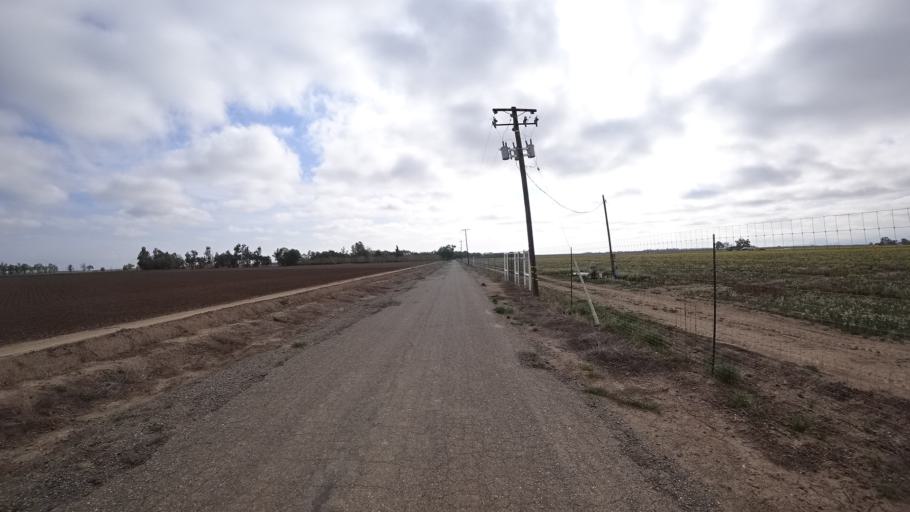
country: US
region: California
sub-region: Colusa County
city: Colusa
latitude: 39.4185
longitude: -121.9751
